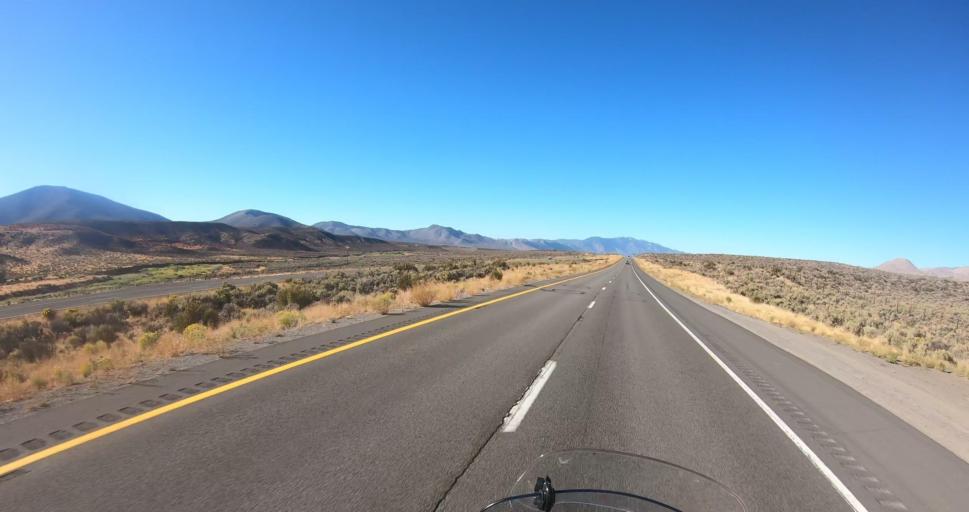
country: US
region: Nevada
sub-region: Washoe County
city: Cold Springs
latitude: 39.7045
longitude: -120.0332
